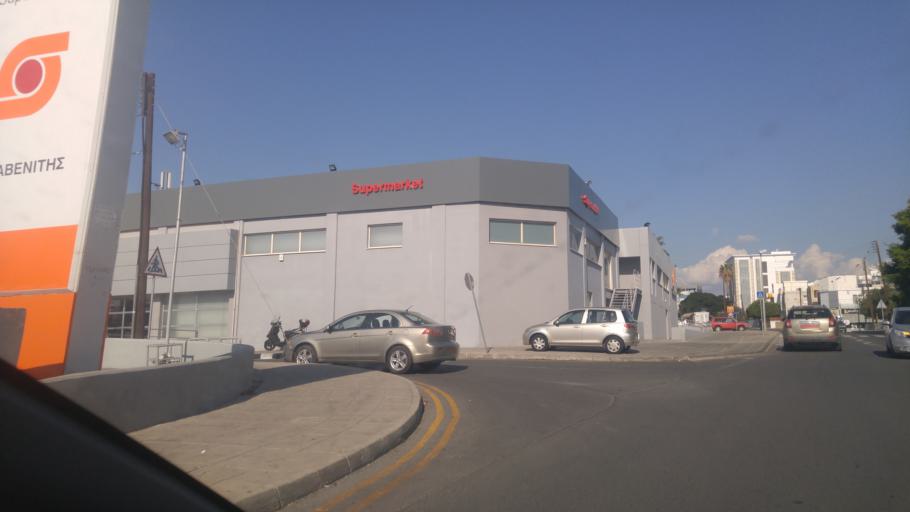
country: CY
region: Limassol
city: Limassol
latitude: 34.6917
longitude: 33.0530
